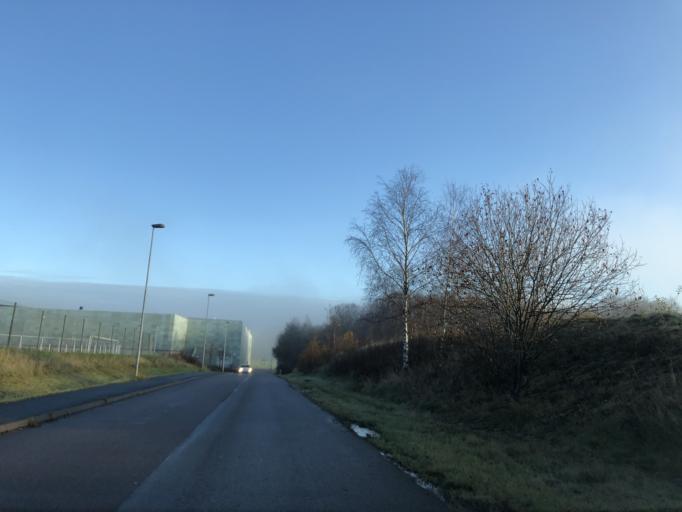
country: SE
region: Vaestra Goetaland
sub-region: Goteborg
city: Rannebergen
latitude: 57.7926
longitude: 12.0537
